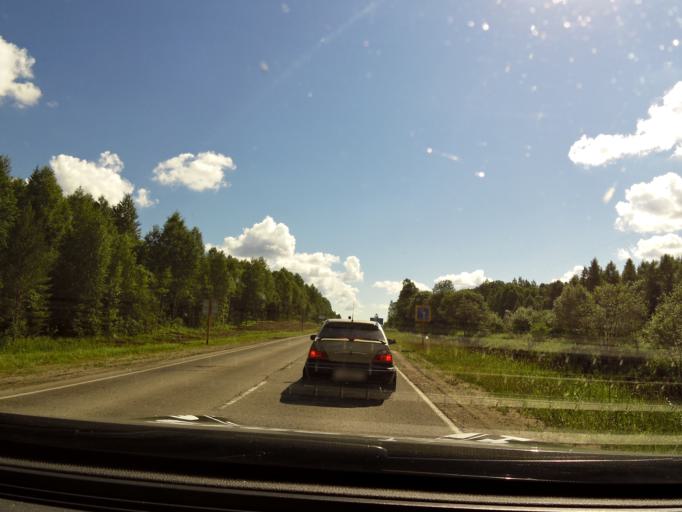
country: RU
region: Vologda
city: Lipin Bor
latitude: 60.2060
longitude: 38.3107
